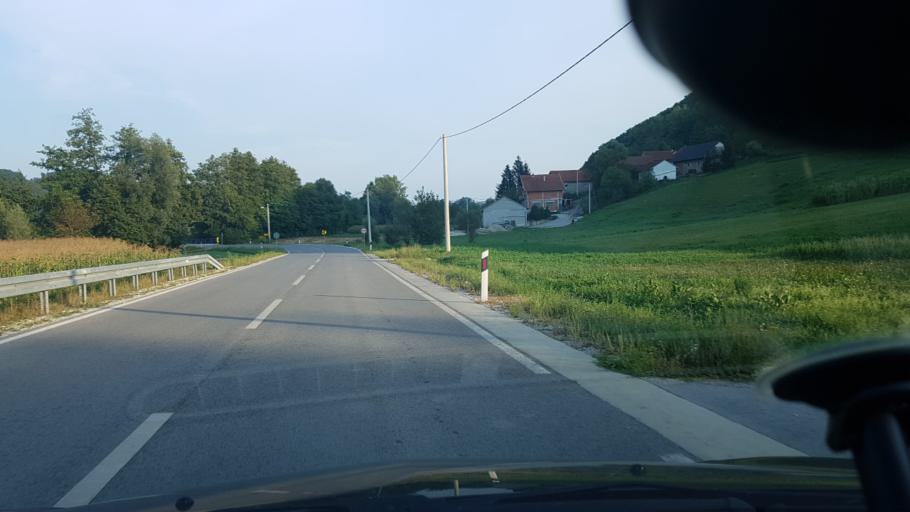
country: HR
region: Krapinsko-Zagorska
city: Pregrada
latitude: 46.1568
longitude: 15.7972
